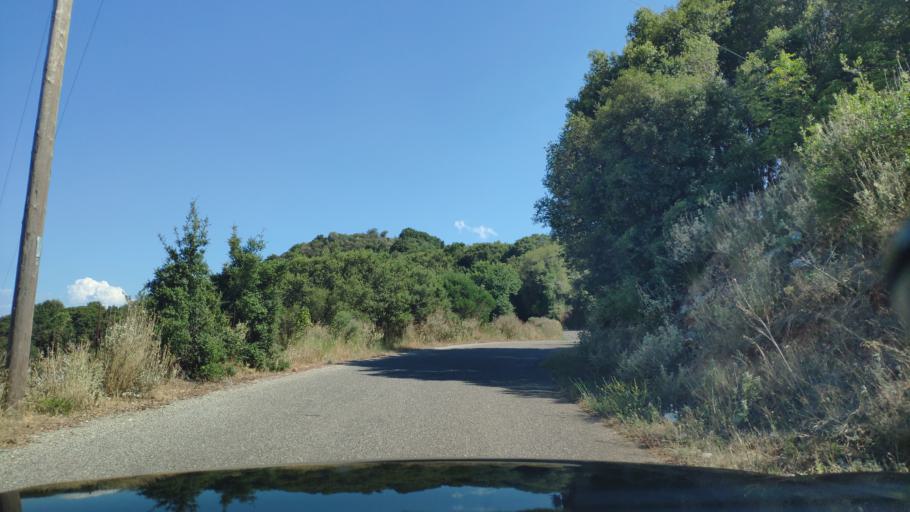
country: GR
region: West Greece
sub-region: Nomos Aitolias kai Akarnanias
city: Katouna
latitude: 38.8073
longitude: 21.1092
